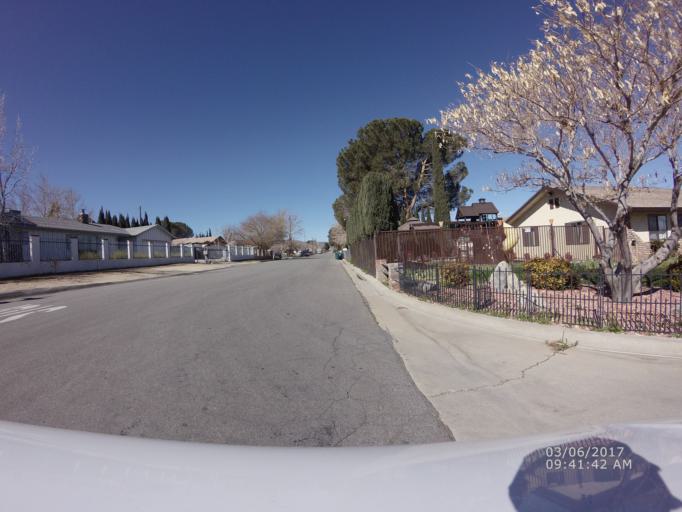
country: US
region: California
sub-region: Los Angeles County
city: Quartz Hill
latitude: 34.6485
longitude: -118.2101
